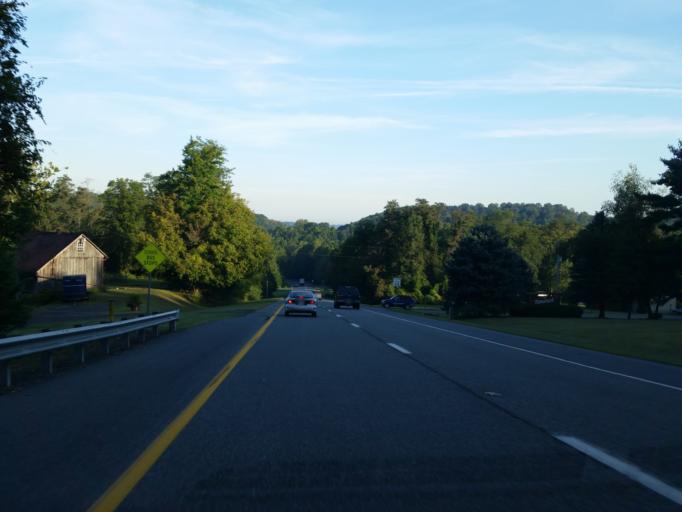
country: US
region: Pennsylvania
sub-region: Lancaster County
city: Willow Street
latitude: 39.9200
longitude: -76.2471
